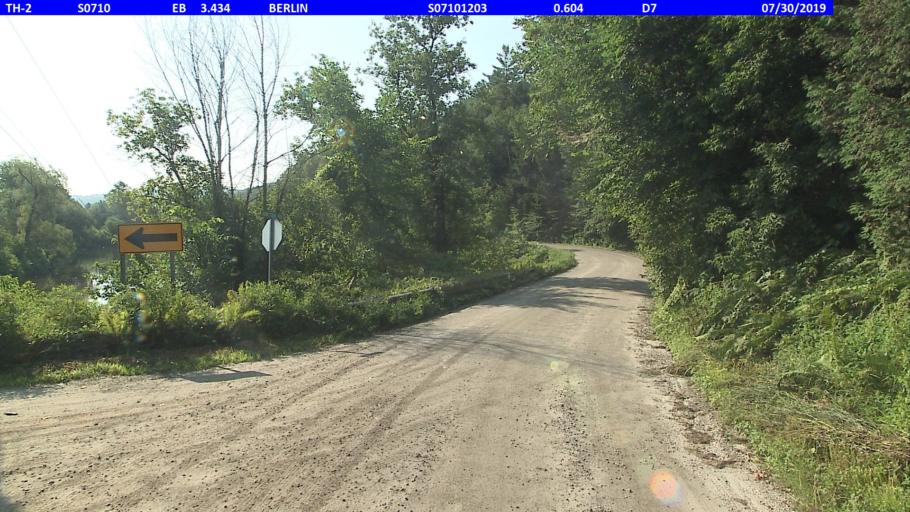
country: US
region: Vermont
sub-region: Washington County
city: Montpelier
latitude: 44.2656
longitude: -72.6296
